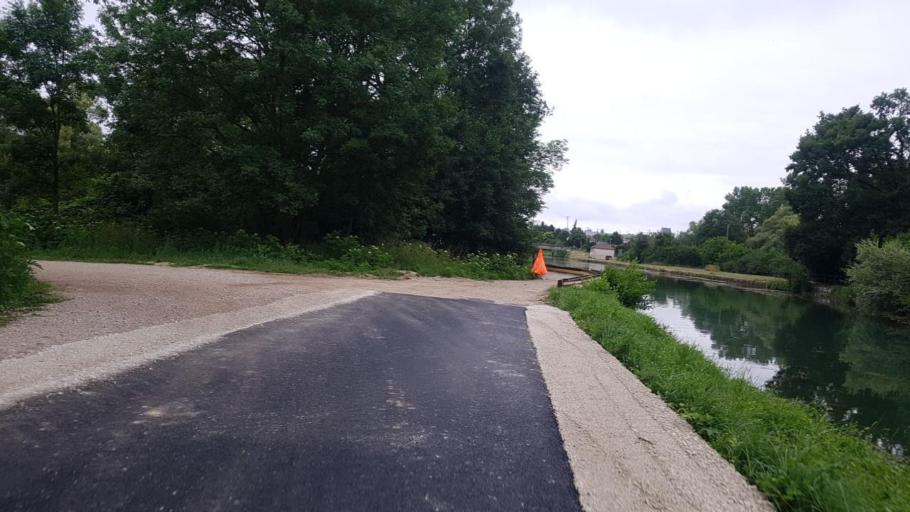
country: FR
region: Champagne-Ardenne
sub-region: Departement de la Marne
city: Vitry-le-Francois
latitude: 48.8320
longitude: 4.5123
